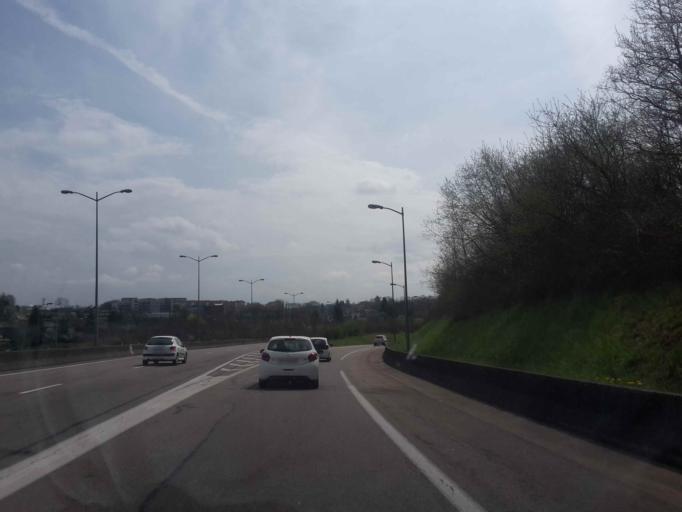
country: FR
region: Franche-Comte
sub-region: Departement du Doubs
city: Besancon
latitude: 47.2653
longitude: 6.0050
